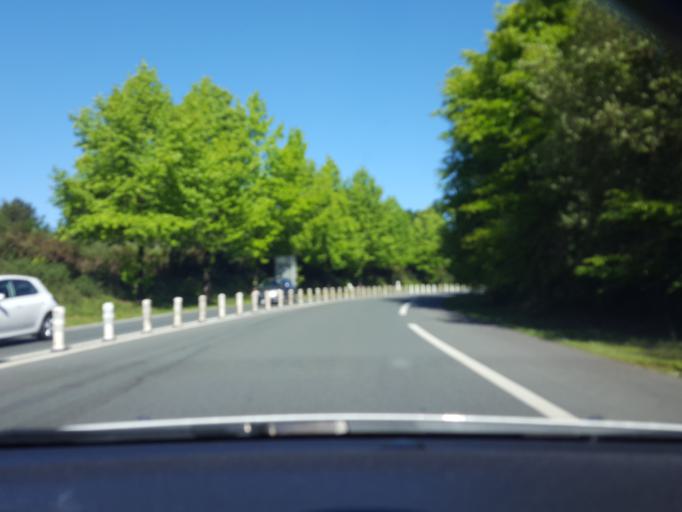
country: FR
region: Aquitaine
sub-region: Departement des Landes
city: Ondres
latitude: 43.5418
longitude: -1.4365
